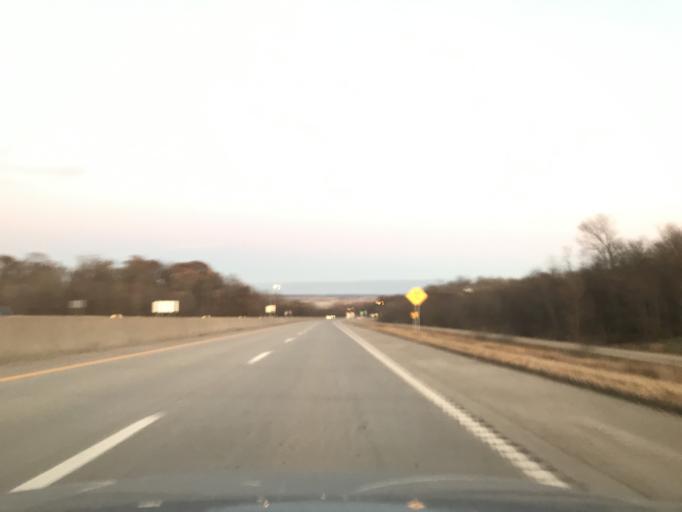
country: US
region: Missouri
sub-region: Marion County
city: Hannibal
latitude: 39.7173
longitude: -91.3715
